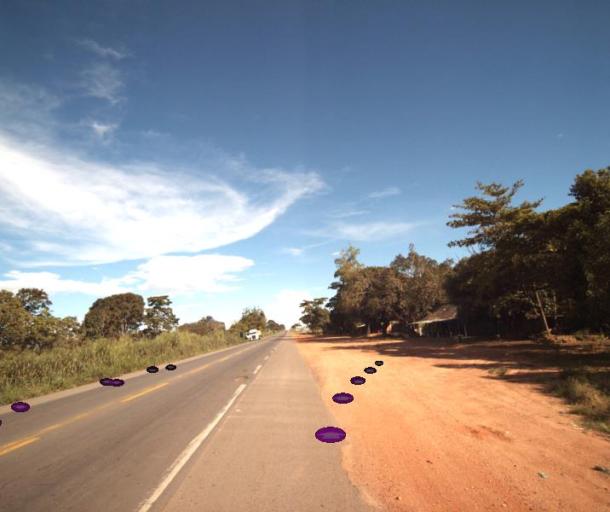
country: BR
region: Goias
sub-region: Rialma
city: Rialma
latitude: -15.4701
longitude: -49.4976
